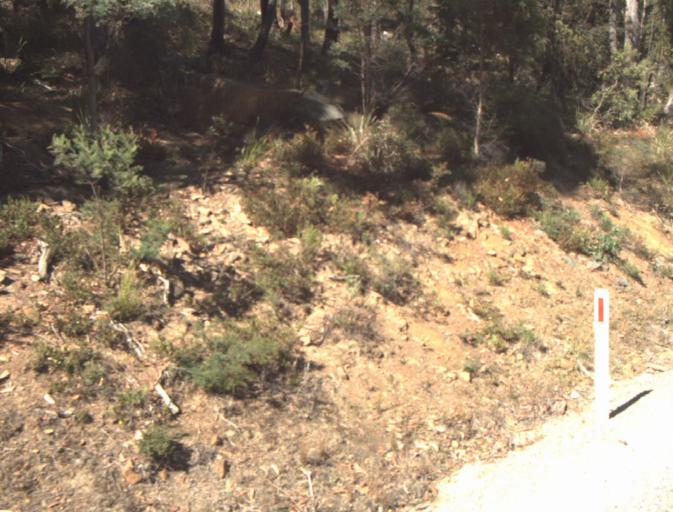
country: AU
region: Tasmania
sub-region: Launceston
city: Mayfield
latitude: -41.3361
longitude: 147.1977
